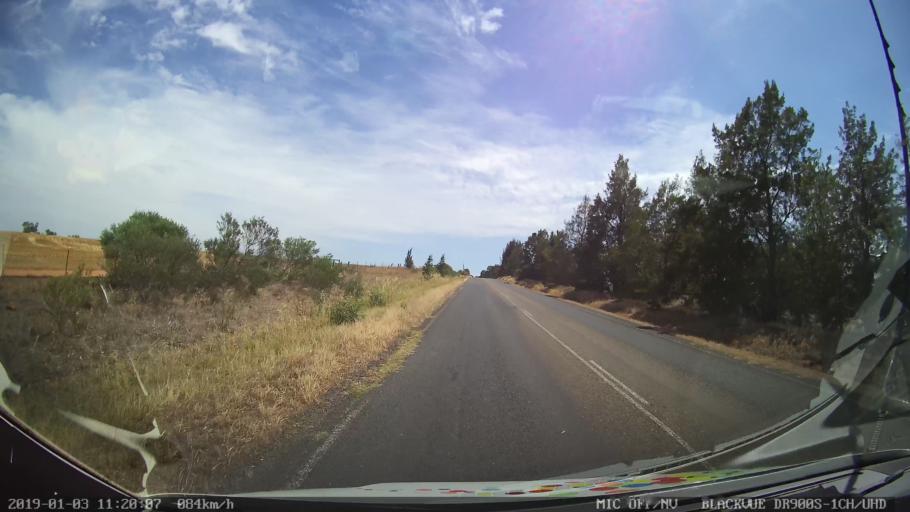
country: AU
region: New South Wales
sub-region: Young
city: Young
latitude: -34.1050
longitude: 148.2552
